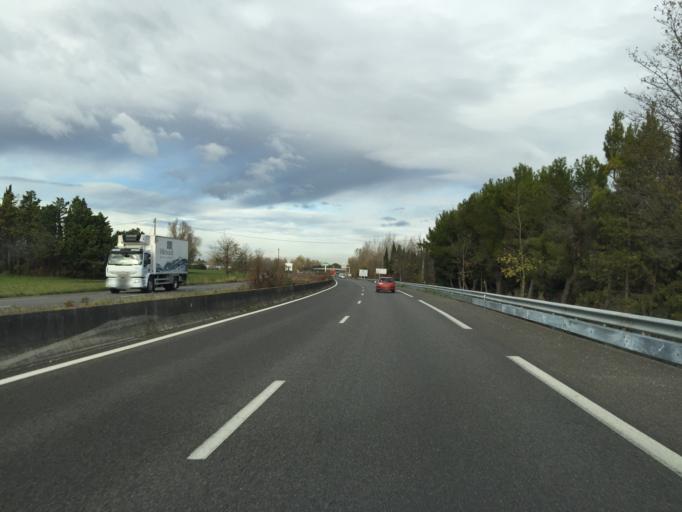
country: FR
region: Provence-Alpes-Cote d'Azur
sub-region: Departement du Vaucluse
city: Althen-des-Paluds
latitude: 44.0015
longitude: 4.9424
